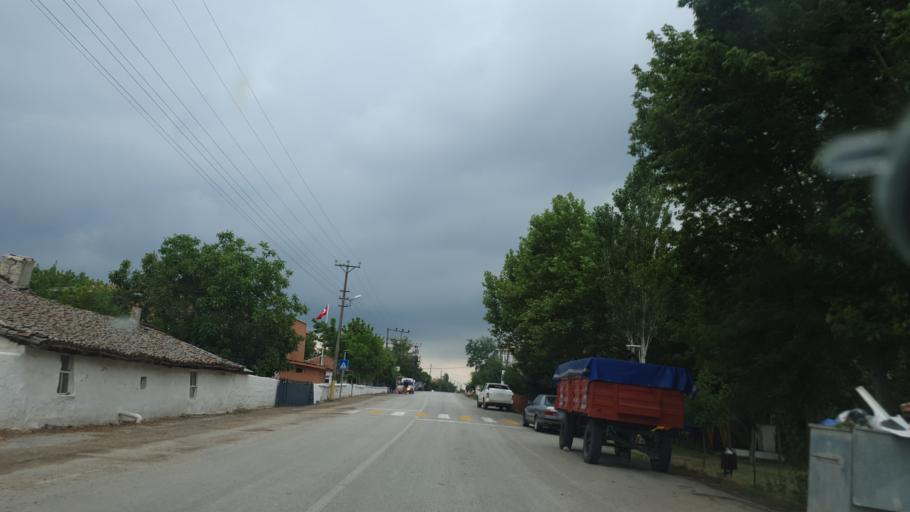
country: TR
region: Tekirdag
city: Hayrabolu
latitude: 41.2197
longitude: 26.9826
